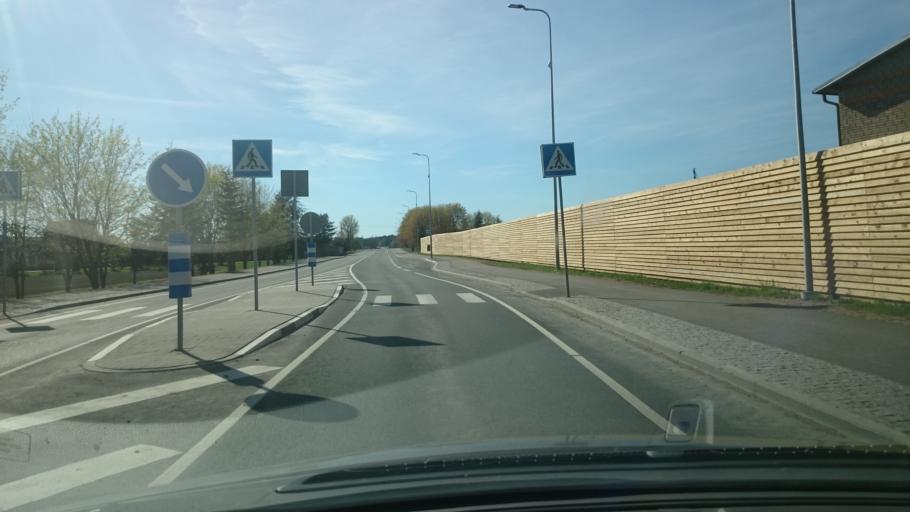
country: EE
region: Laeaene-Virumaa
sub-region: Kadrina vald
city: Kadrina
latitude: 59.3519
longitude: 26.2176
